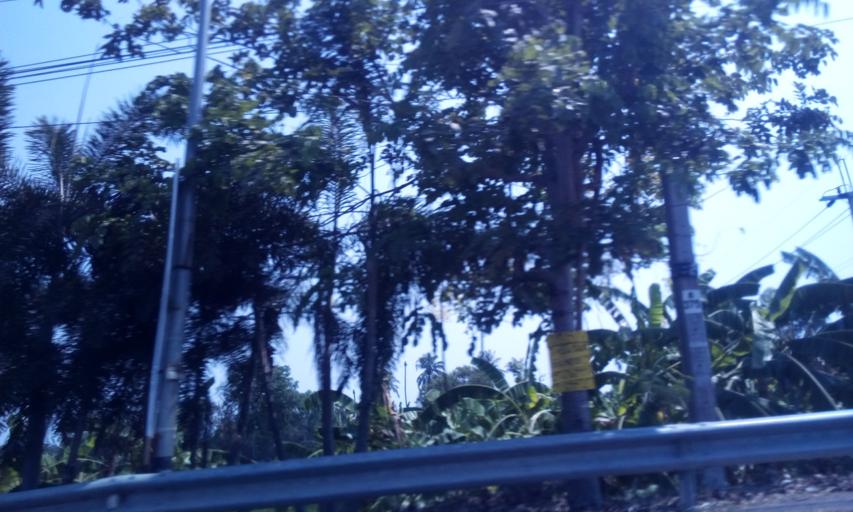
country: TH
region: Nonthaburi
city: Bang Bua Thong
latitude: 13.9097
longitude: 100.3582
